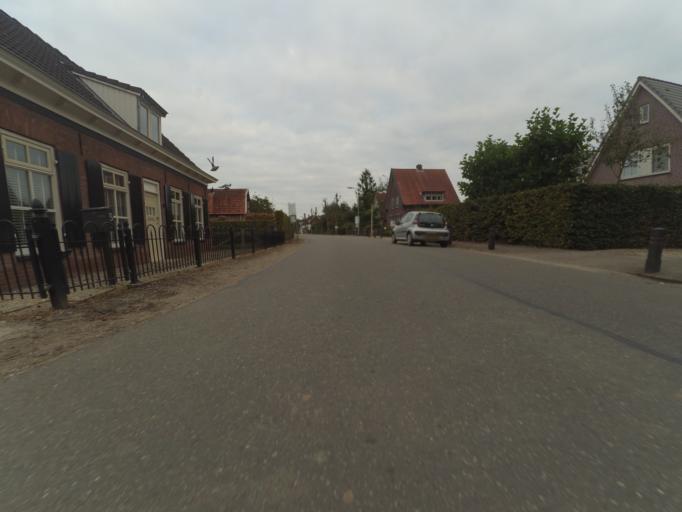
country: NL
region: Gelderland
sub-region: Gemeente Culemborg
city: Culemborg
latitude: 51.9543
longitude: 5.2847
